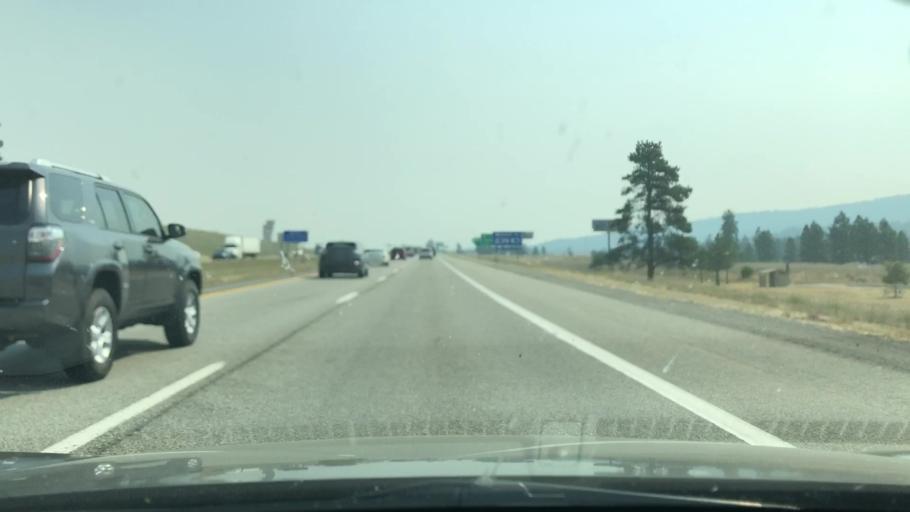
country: US
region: Washington
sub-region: Spokane County
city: Otis Orchards-East Farms
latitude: 47.6972
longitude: -117.0379
